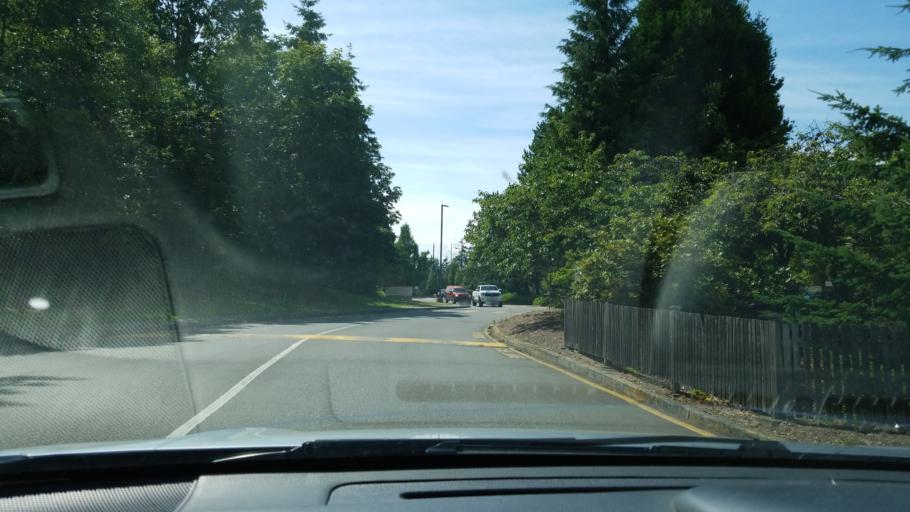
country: US
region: Washington
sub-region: Snohomish County
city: Lynnwood
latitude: 47.8141
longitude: -122.3258
